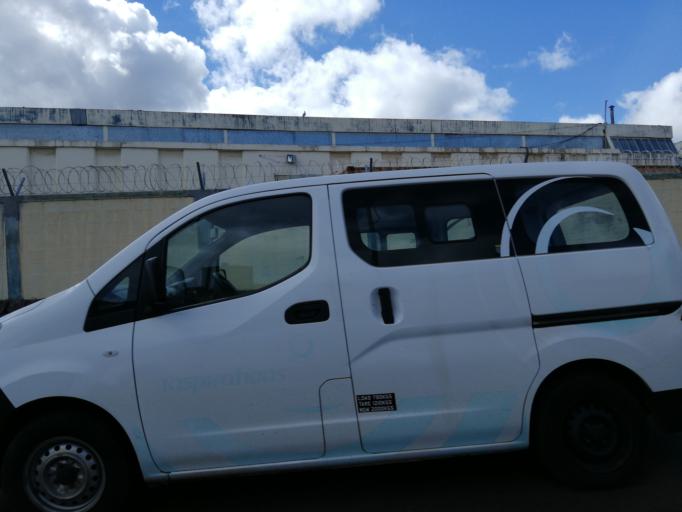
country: MU
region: Moka
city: Pailles
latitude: -20.1877
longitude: 57.4669
